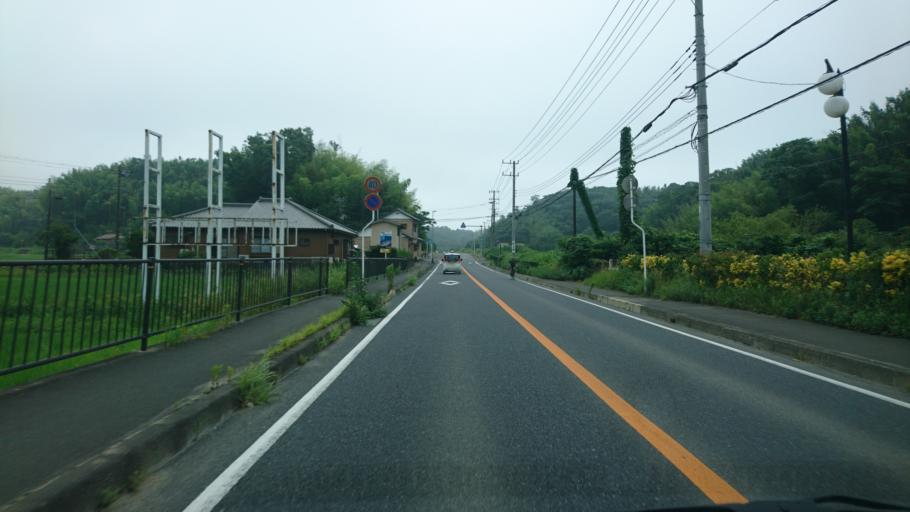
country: JP
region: Chiba
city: Kimitsu
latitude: 35.2573
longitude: 139.8840
